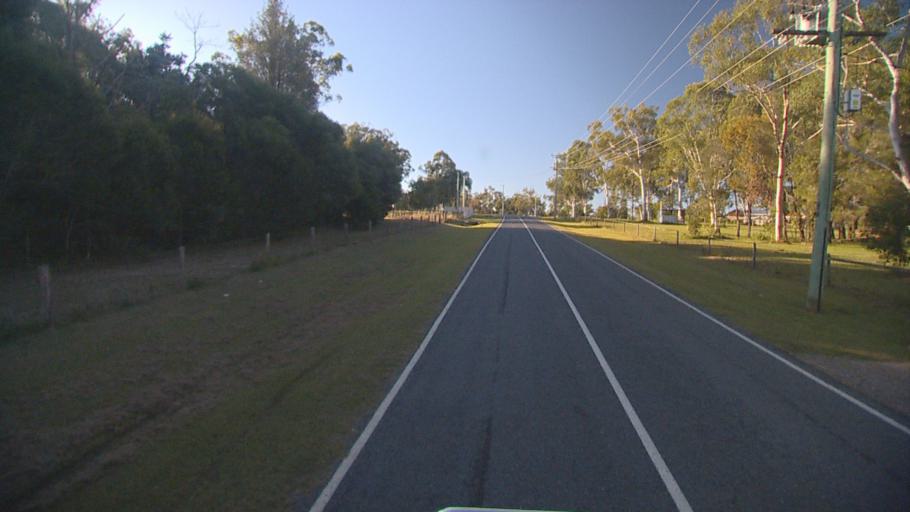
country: AU
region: Queensland
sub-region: Redland
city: Redland Bay
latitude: -27.6624
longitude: 153.2770
